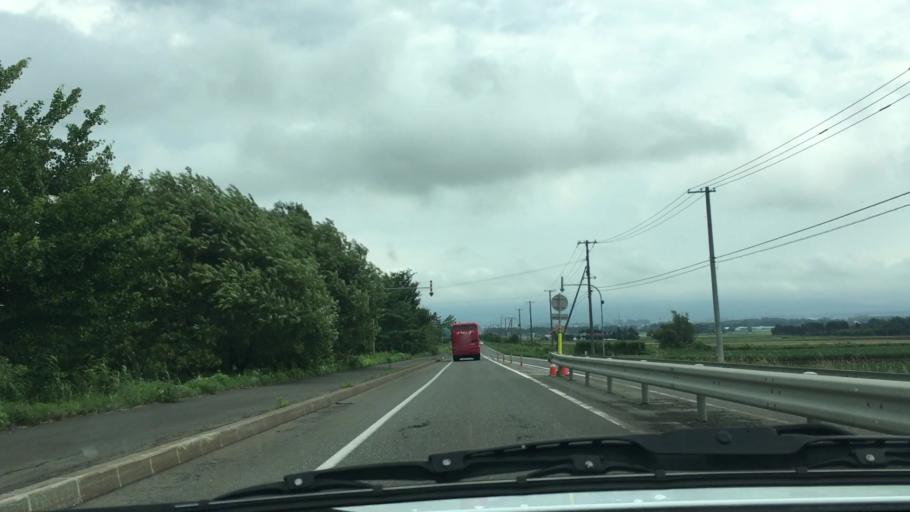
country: JP
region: Hokkaido
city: Chitose
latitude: 42.9470
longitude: 141.7719
